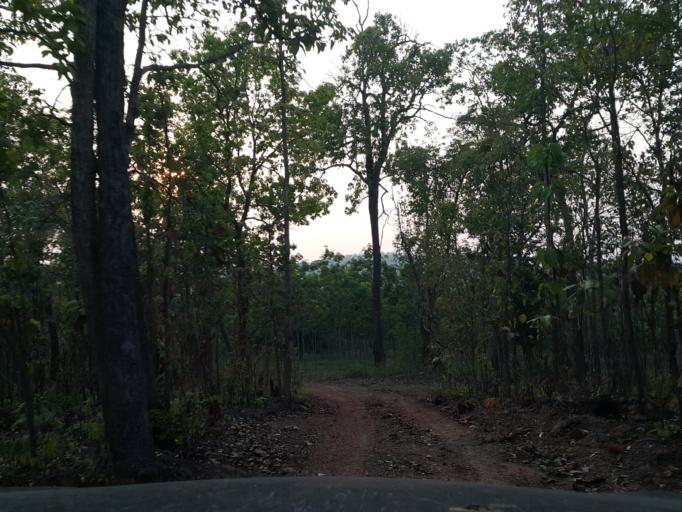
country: TH
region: Lamphun
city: Thung Hua Chang
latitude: 17.9121
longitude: 99.0777
